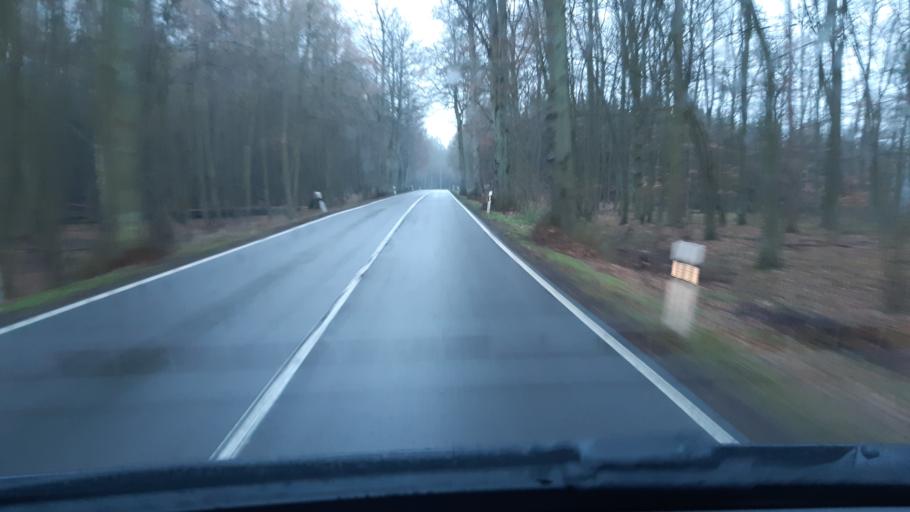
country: DE
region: Brandenburg
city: Mittenwalde
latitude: 53.1666
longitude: 13.6501
